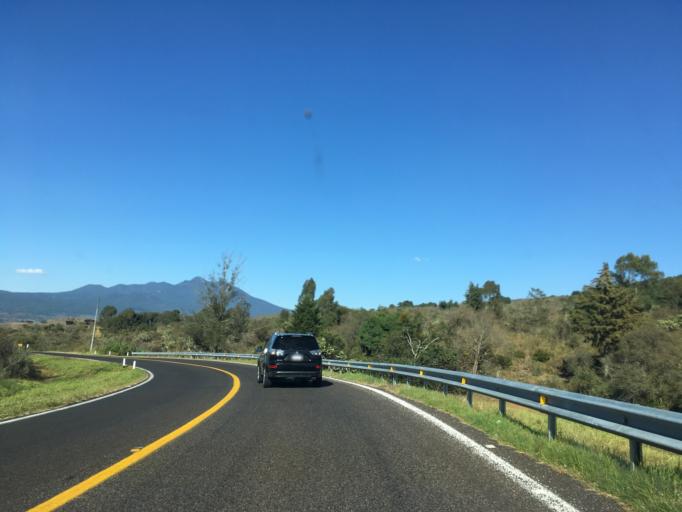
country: MX
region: Michoacan
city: Tzintzuntzan
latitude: 19.6154
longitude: -101.5769
